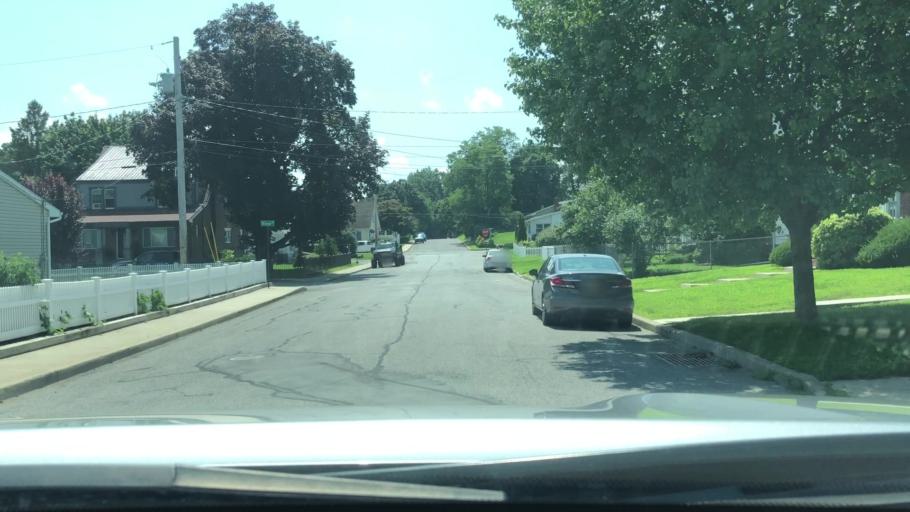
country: US
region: New York
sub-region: Dutchess County
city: Beacon
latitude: 41.5025
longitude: -73.9714
